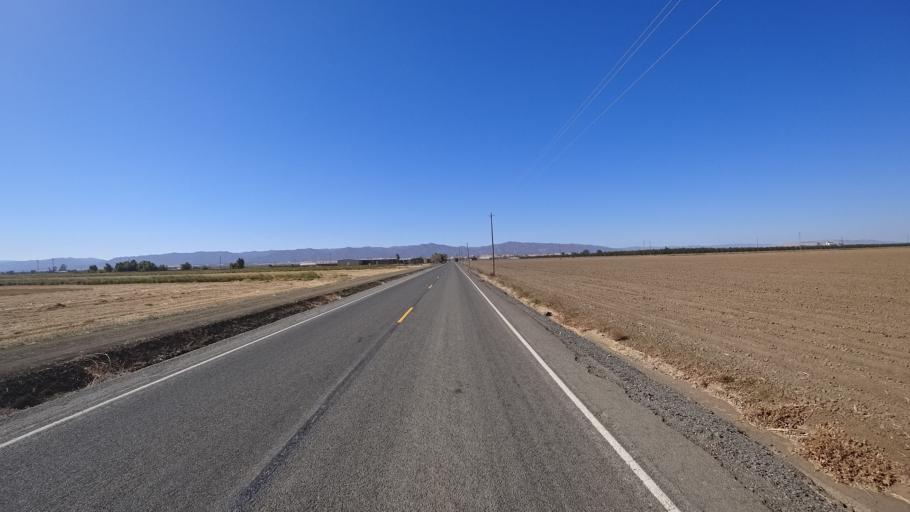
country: US
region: California
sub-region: Yolo County
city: Cottonwood
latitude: 38.6204
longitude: -121.9584
